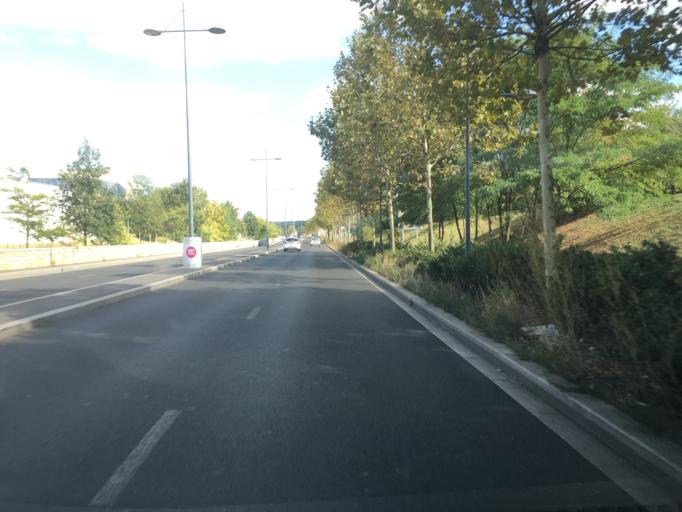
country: FR
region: Ile-de-France
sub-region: Departement du Val-de-Marne
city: Bonneuil-sur-Marne
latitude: 48.7662
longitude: 2.4739
